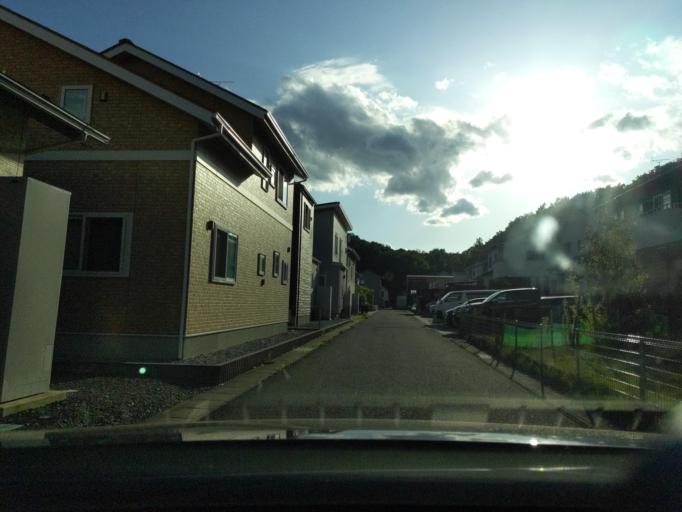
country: JP
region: Fukushima
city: Miharu
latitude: 37.4293
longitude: 140.4295
